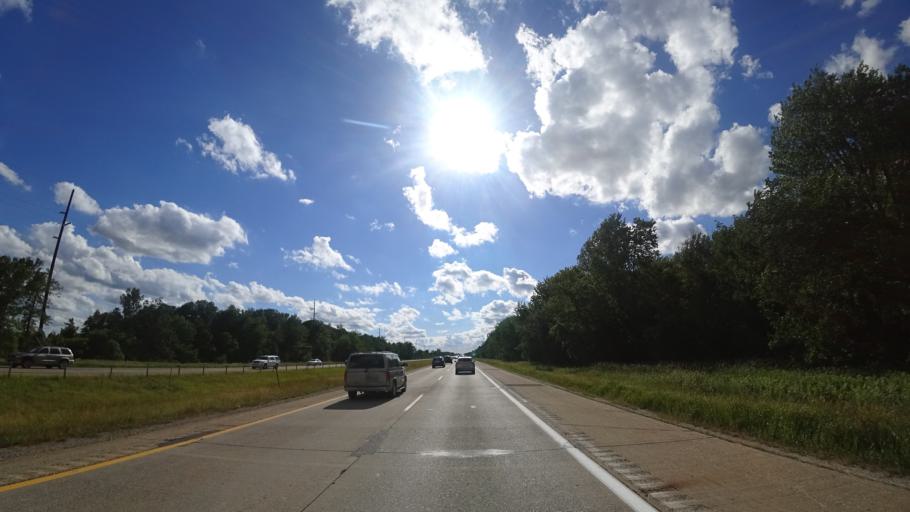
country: US
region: Michigan
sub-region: Ionia County
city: Portland
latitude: 42.8792
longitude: -85.0033
